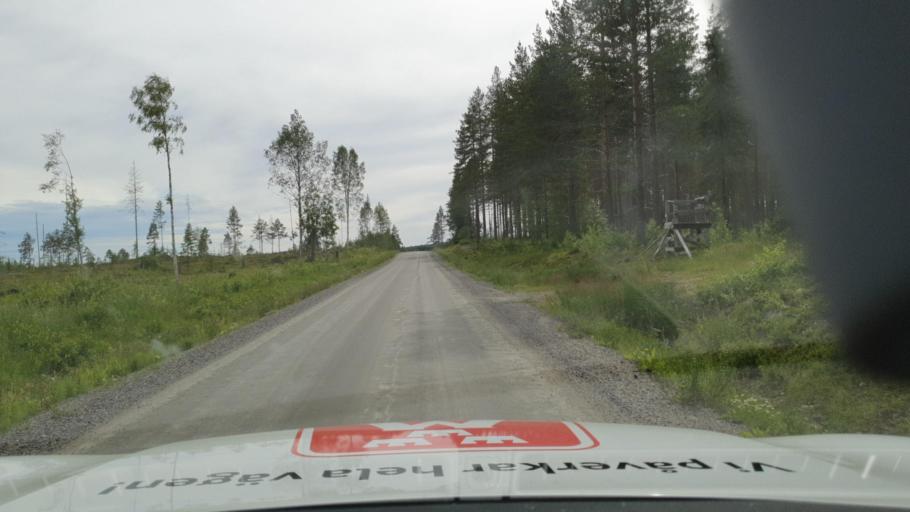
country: SE
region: Vaesterbotten
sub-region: Skelleftea Kommun
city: Burea
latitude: 64.4188
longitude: 21.0077
